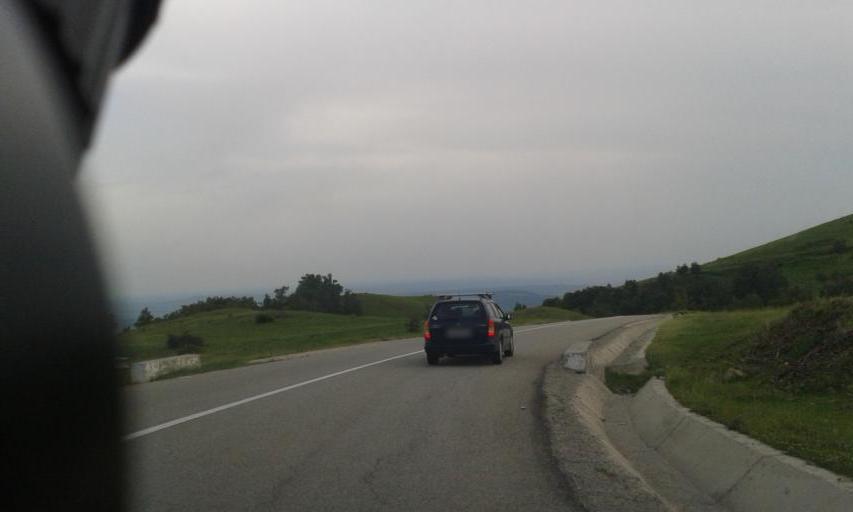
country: RO
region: Gorj
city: Novaci-Straini
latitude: 45.2184
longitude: 23.6991
